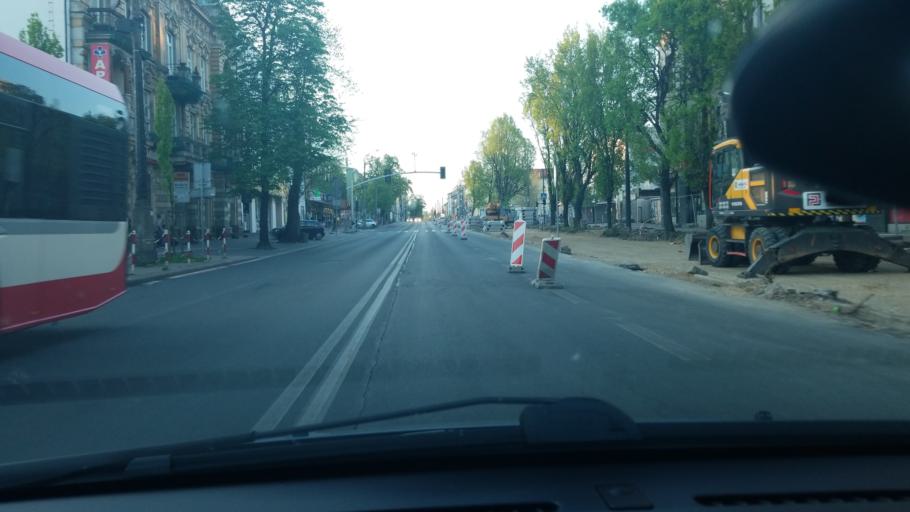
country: PL
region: Silesian Voivodeship
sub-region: Czestochowa
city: Czestochowa
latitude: 50.8099
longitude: 19.1181
